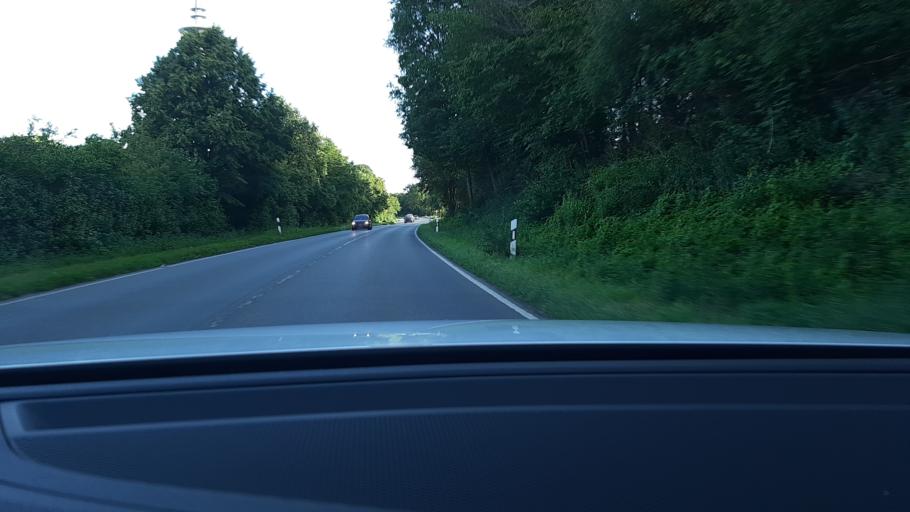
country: DE
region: Schleswig-Holstein
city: Stockelsdorf
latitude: 53.9114
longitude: 10.6406
